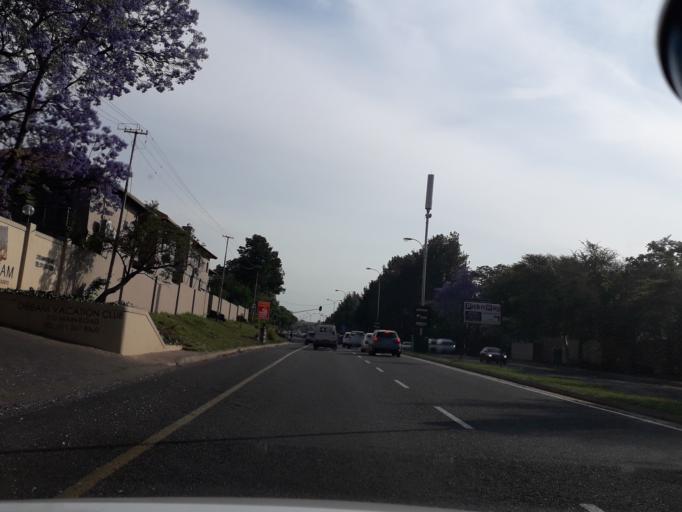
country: ZA
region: Gauteng
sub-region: City of Johannesburg Metropolitan Municipality
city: Johannesburg
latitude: -26.0694
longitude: 28.0167
